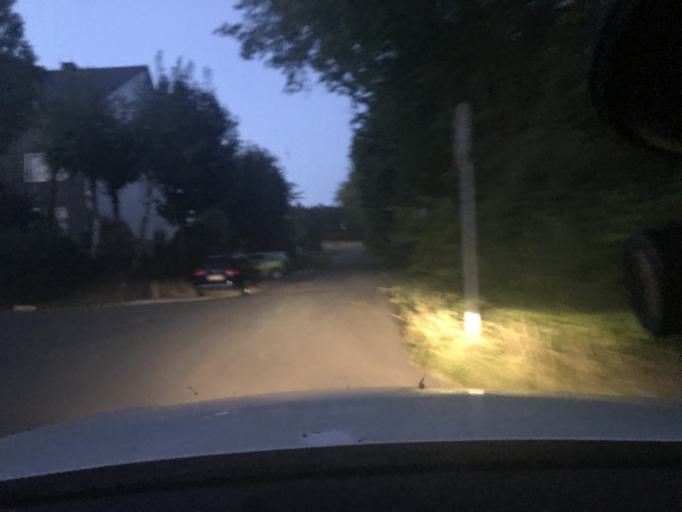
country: DE
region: Bavaria
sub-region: Upper Palatinate
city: Auerbach
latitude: 49.7214
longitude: 11.6213
